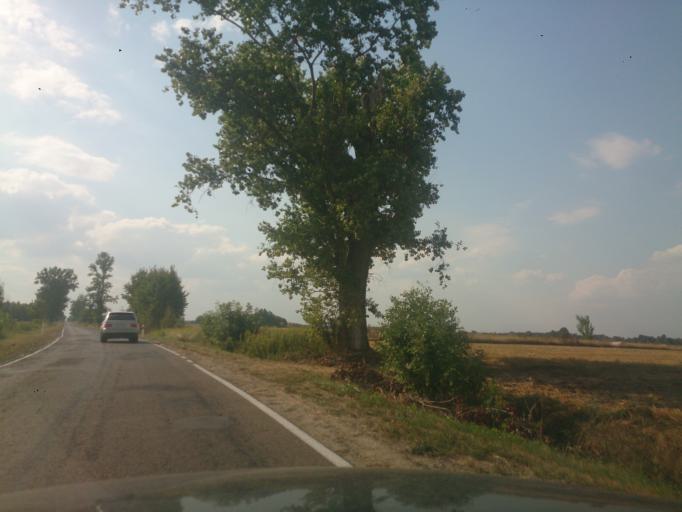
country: PL
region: Swietokrzyskie
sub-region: Powiat sandomierski
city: Klimontow
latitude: 50.6911
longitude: 21.3768
